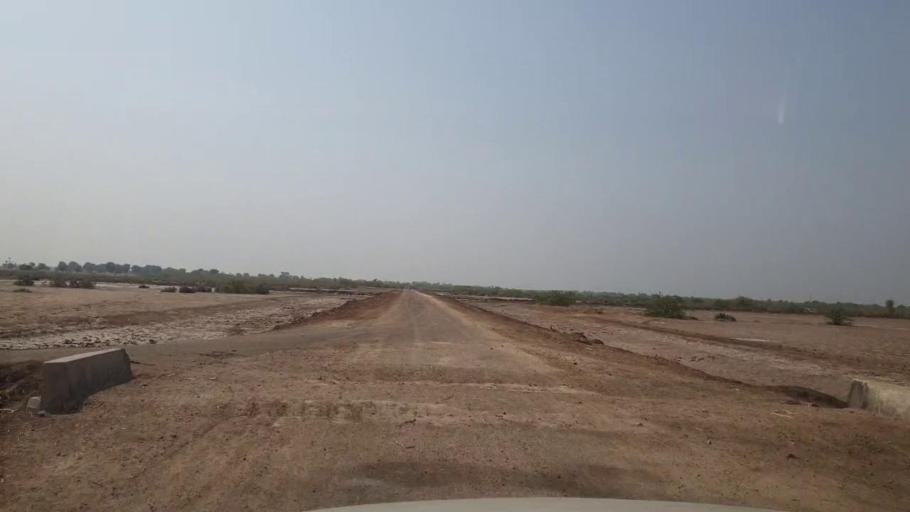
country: PK
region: Sindh
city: Umarkot
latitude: 25.4474
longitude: 69.6913
